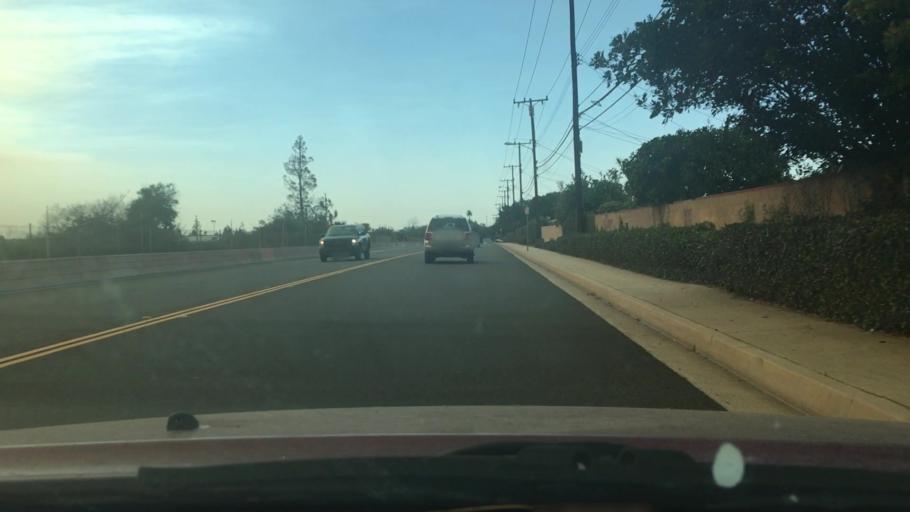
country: US
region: California
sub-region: Los Angeles County
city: La Mirada
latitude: 33.8907
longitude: -118.0164
